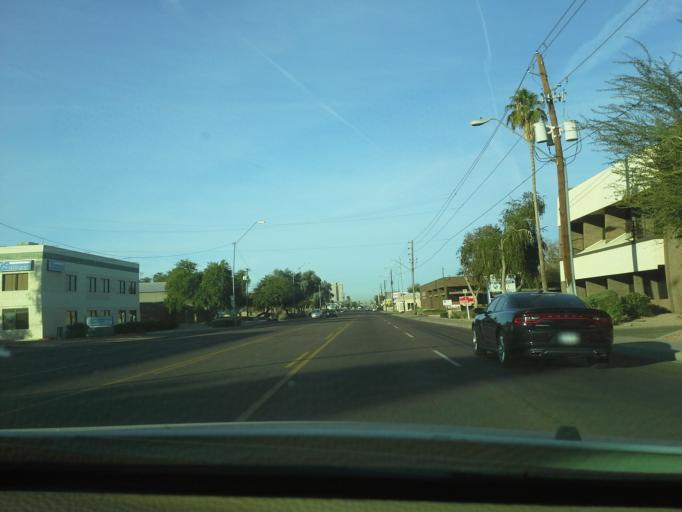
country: US
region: Arizona
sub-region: Maricopa County
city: Phoenix
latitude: 33.4948
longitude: -112.0504
